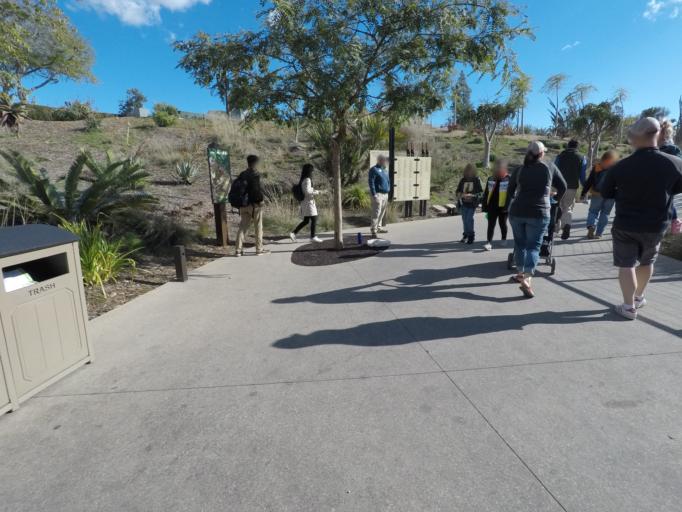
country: US
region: California
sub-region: San Diego County
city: San Diego
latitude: 32.7387
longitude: -117.1500
